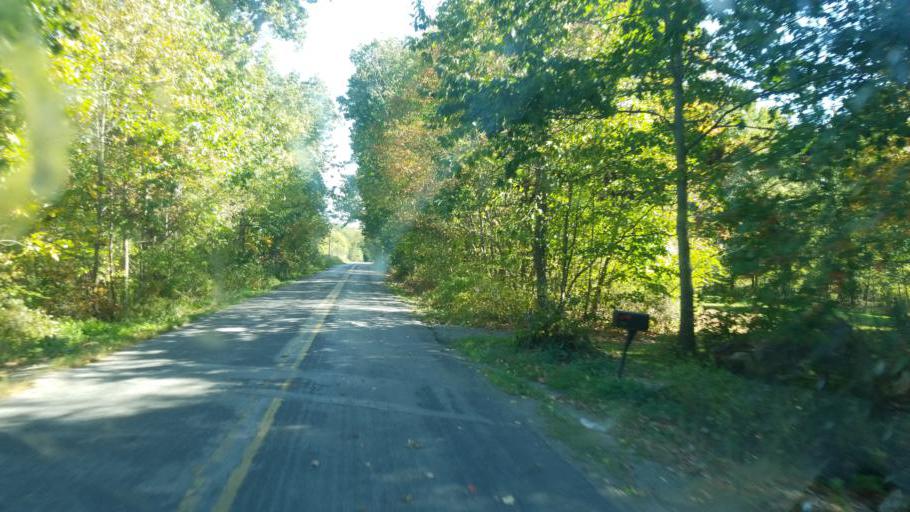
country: US
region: Pennsylvania
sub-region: Mercer County
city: Greenville
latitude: 41.3828
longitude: -80.4237
